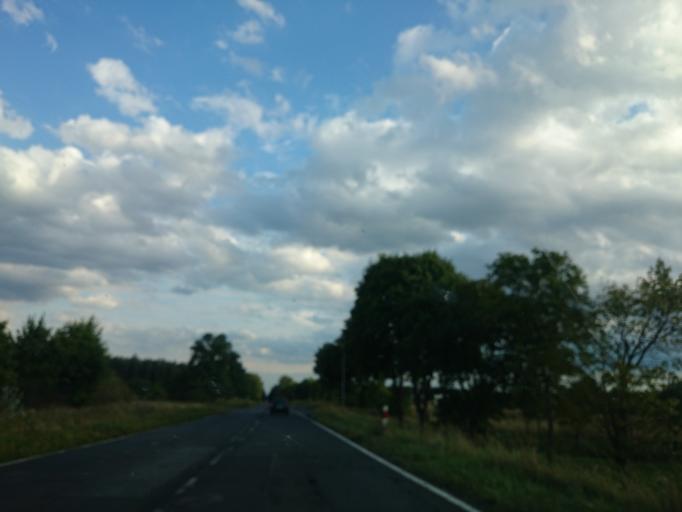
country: PL
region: West Pomeranian Voivodeship
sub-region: Powiat mysliborski
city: Nowogrodek Pomorski
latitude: 52.8758
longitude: 15.0094
